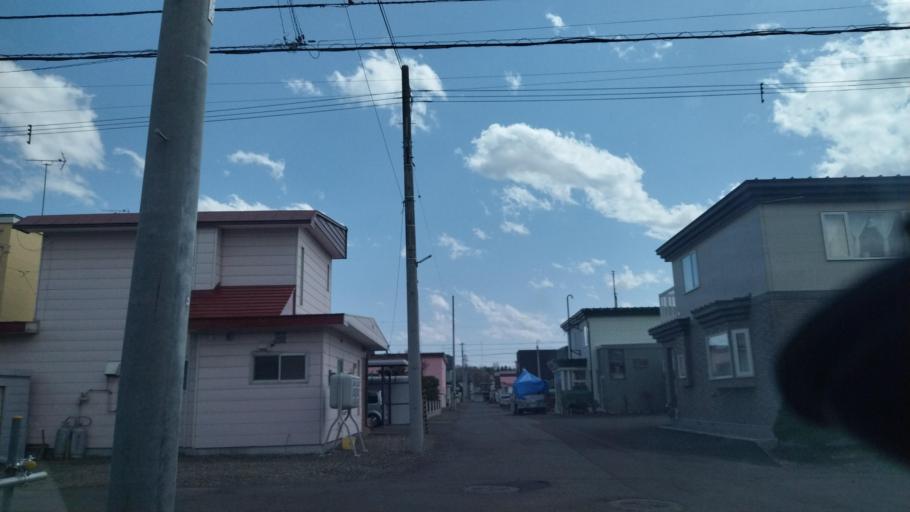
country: JP
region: Hokkaido
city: Obihiro
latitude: 42.9078
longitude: 143.1574
